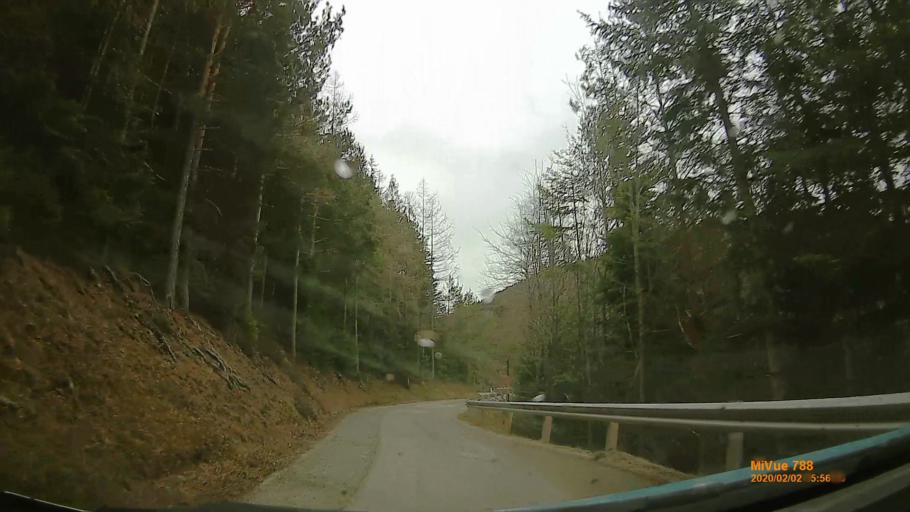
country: AT
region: Lower Austria
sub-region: Politischer Bezirk Neunkirchen
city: Semmering
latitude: 47.6683
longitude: 15.7837
